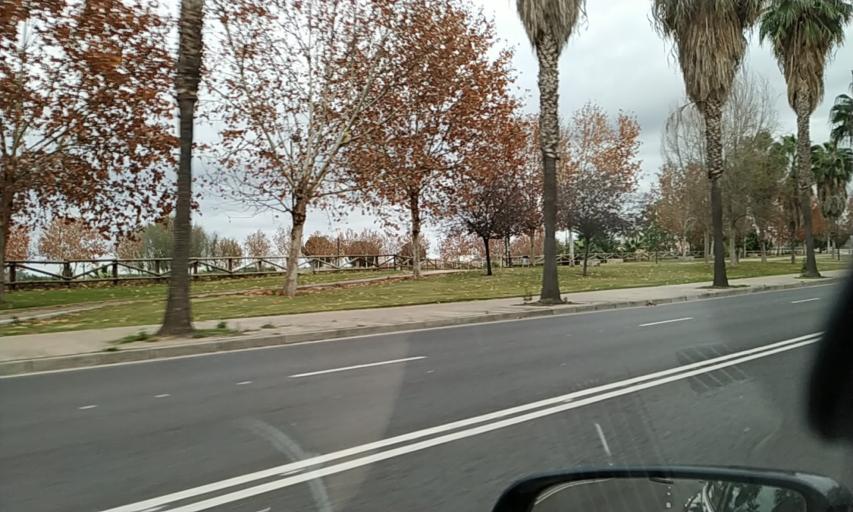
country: ES
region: Extremadura
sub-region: Provincia de Badajoz
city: Badajoz
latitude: 38.8837
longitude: -6.9661
